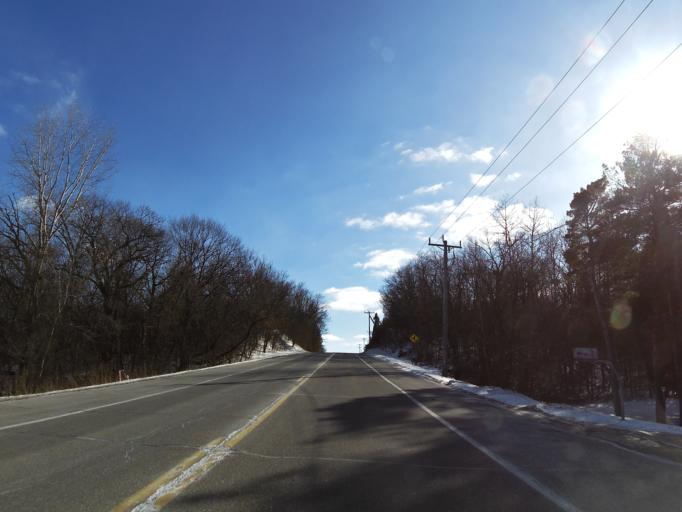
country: US
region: Minnesota
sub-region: Washington County
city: Lake Elmo
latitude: 44.9302
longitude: -92.8627
